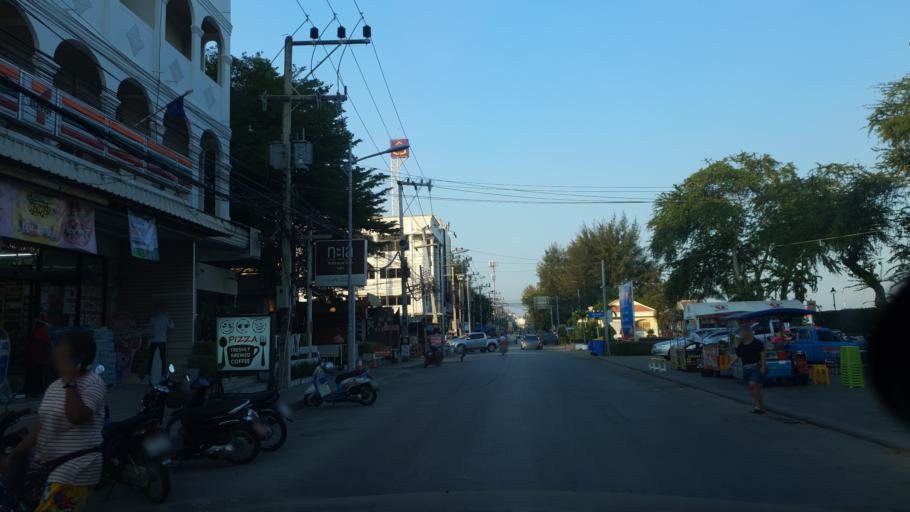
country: TH
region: Phetchaburi
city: Cha-am
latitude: 12.7939
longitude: 99.9836
